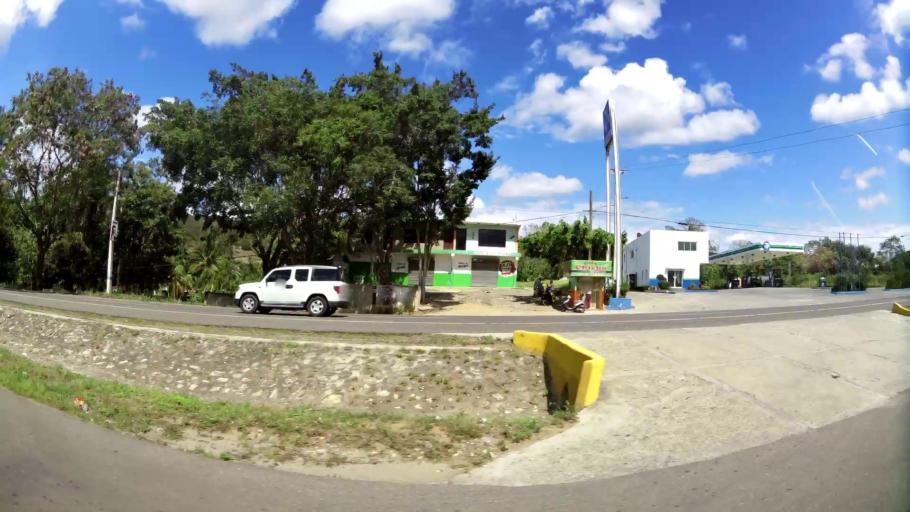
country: DO
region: La Vega
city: Rio Verde Arriba
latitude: 19.2892
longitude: -70.5751
